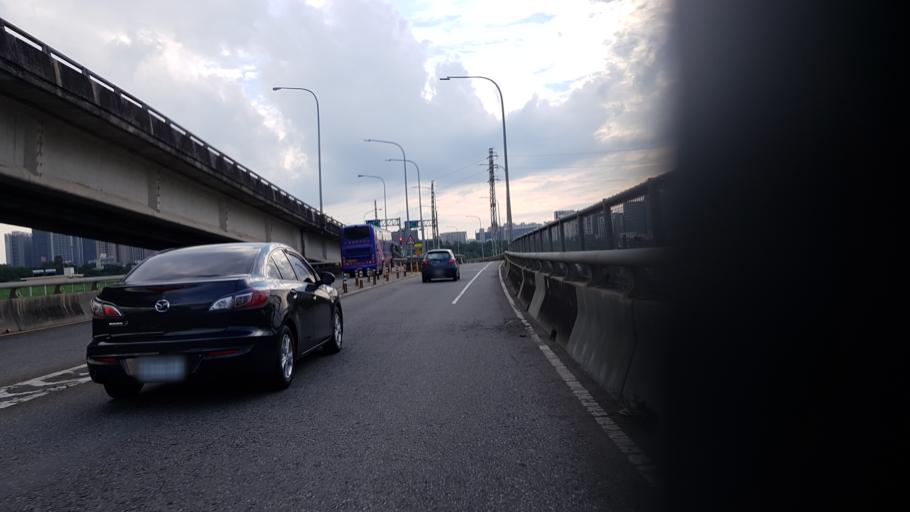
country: TW
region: Taiwan
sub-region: Hsinchu
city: Zhubei
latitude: 24.8039
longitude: 121.0155
